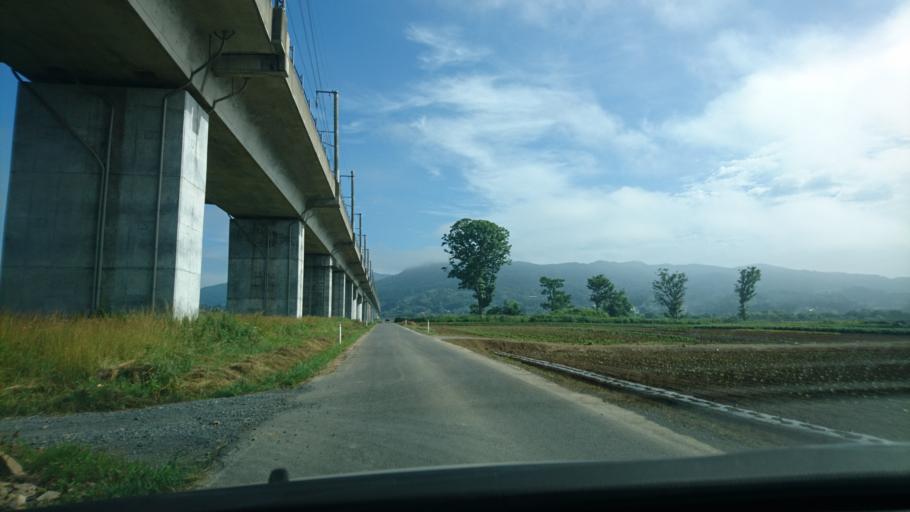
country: JP
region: Iwate
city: Ichinoseki
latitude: 38.9613
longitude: 141.1519
